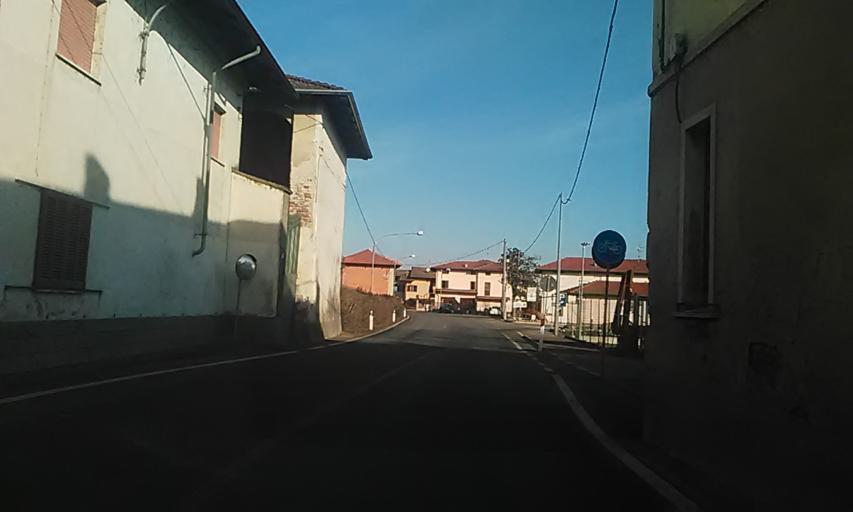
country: IT
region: Piedmont
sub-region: Provincia di Vercelli
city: Balocco
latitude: 45.4563
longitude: 8.2805
